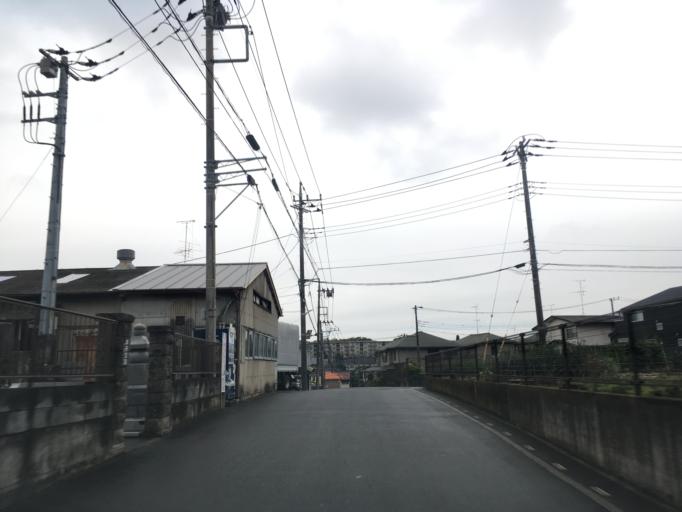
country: JP
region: Saitama
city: Tokorozawa
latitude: 35.7879
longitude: 139.4347
